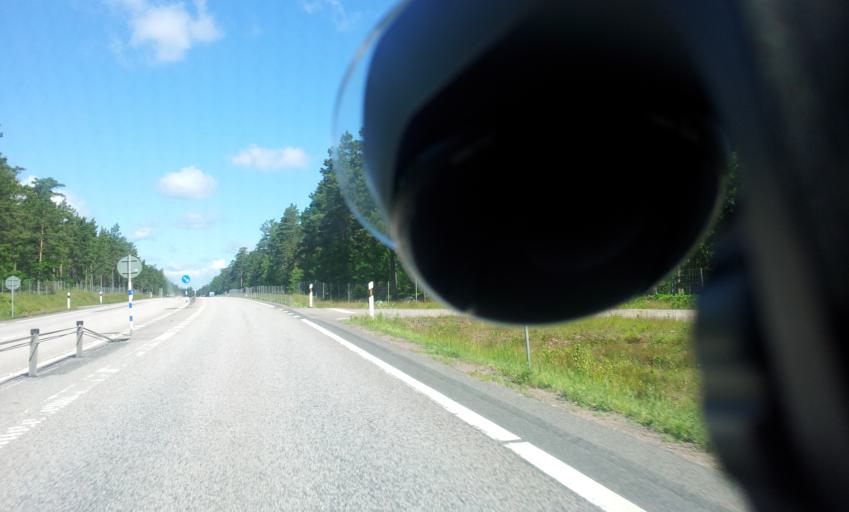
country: SE
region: Kalmar
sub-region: Oskarshamns Kommun
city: Paskallavik
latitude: 57.1158
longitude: 16.4978
